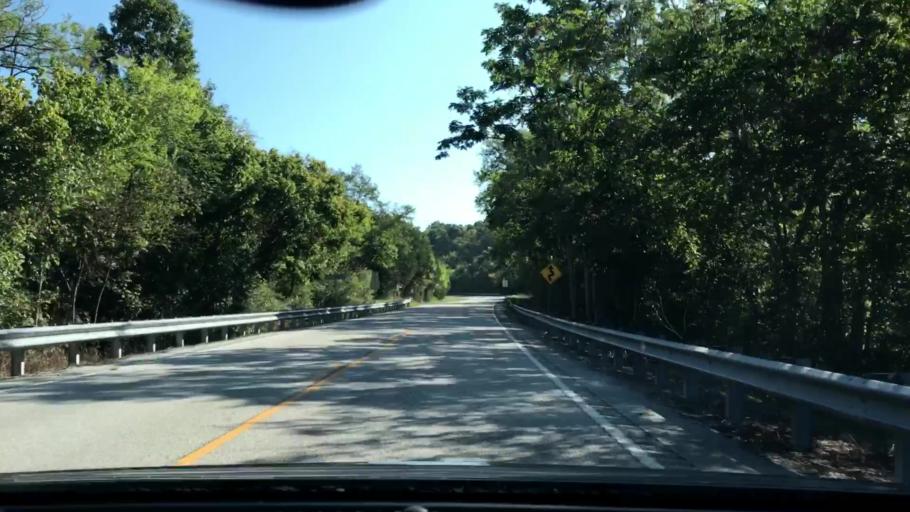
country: US
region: Tennessee
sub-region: Jackson County
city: Gainesboro
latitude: 36.3622
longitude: -85.7725
